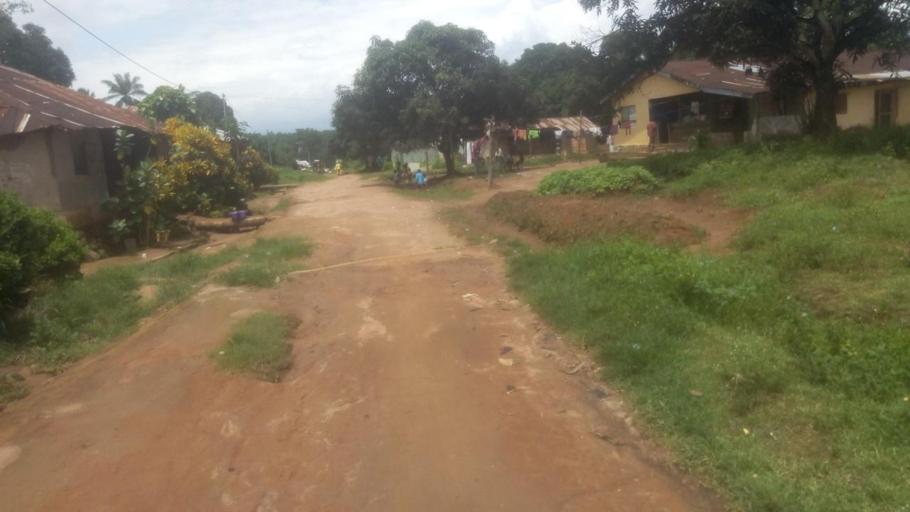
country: SL
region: Northern Province
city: Masoyila
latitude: 8.6002
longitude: -13.2020
